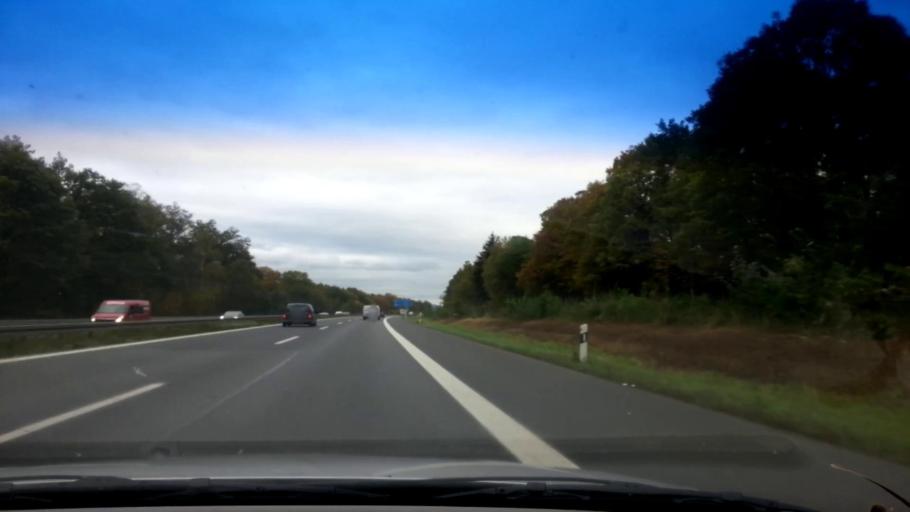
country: DE
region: Bavaria
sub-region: Upper Franconia
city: Kemmern
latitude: 49.9500
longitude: 10.8969
